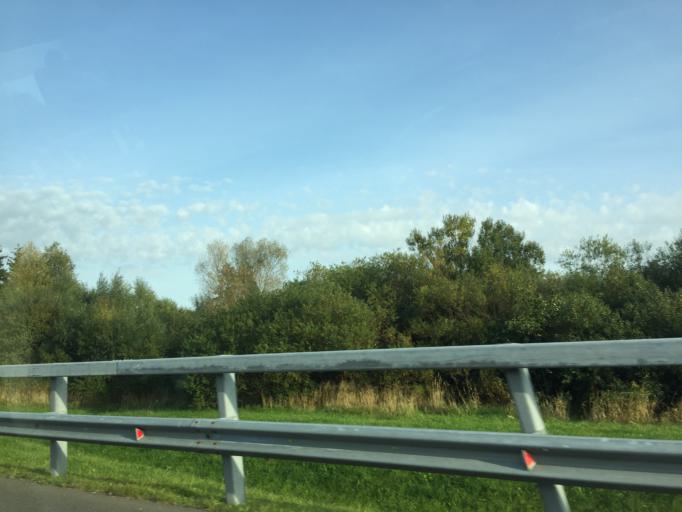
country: RU
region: Kaliningrad
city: Gur'yevsk
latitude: 54.8763
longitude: 20.5826
